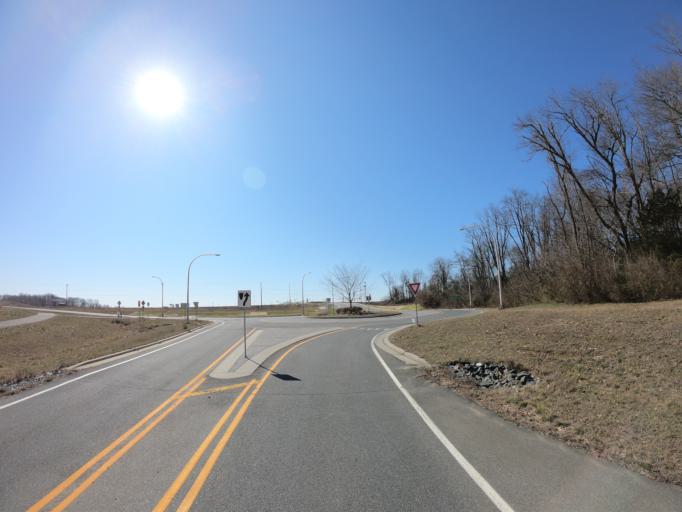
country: US
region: Delaware
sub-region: New Castle County
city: Middletown
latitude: 39.5276
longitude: -75.6793
